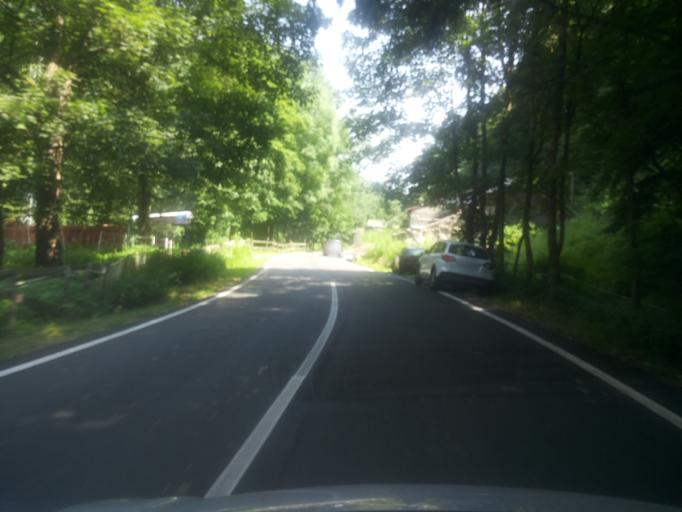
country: IT
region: Piedmont
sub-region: Provincia di Biella
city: Rosazza
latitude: 45.6807
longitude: 7.9719
